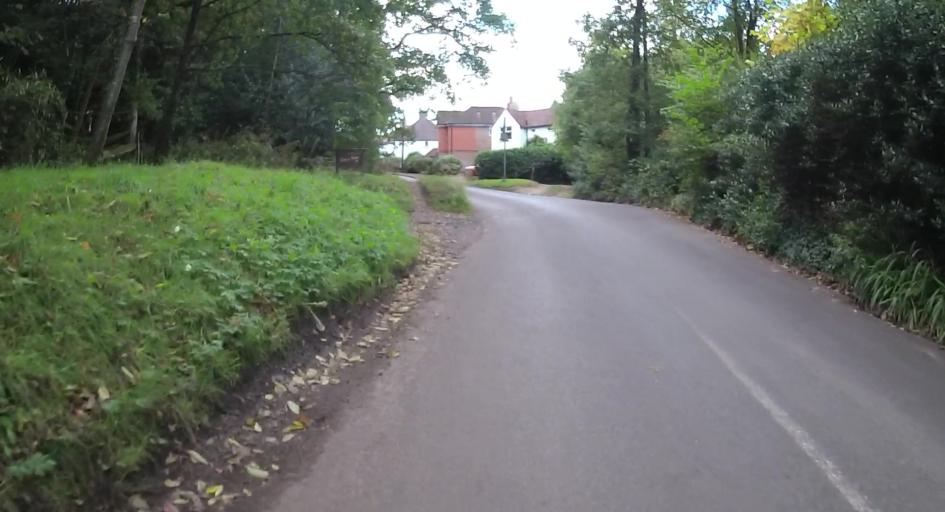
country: GB
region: England
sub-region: Surrey
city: Farnham
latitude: 51.1953
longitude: -0.8044
